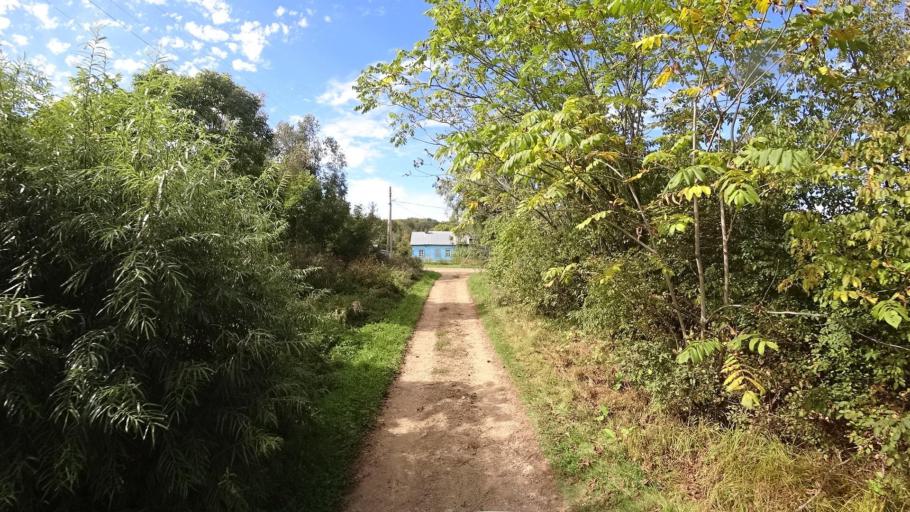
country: RU
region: Primorskiy
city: Yakovlevka
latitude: 44.3964
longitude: 133.6002
